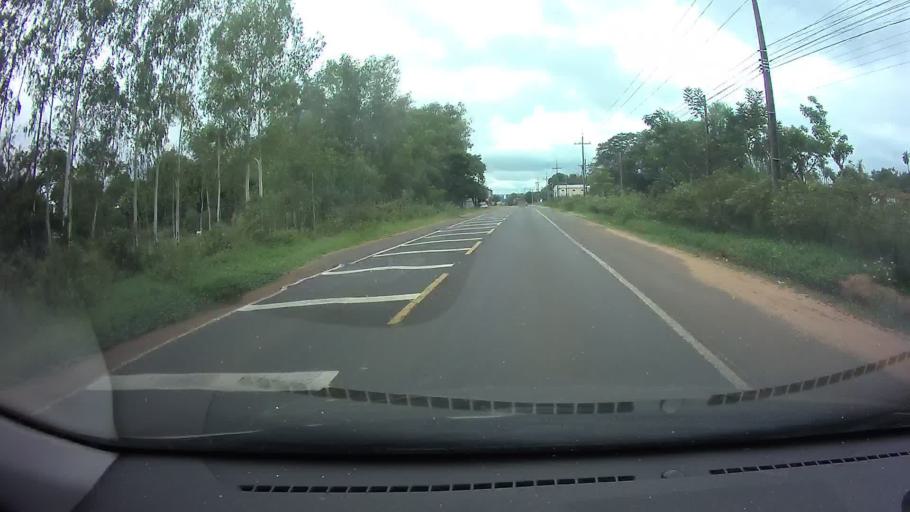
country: PY
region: Central
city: Guarambare
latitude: -25.5006
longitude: -57.4899
